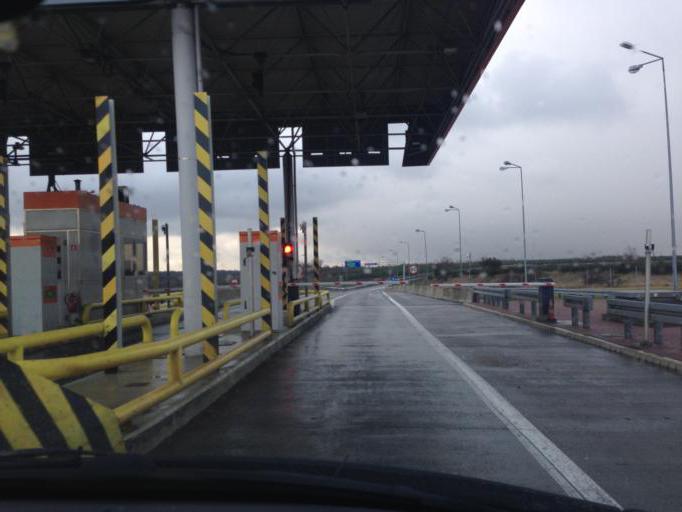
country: PL
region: Opole Voivodeship
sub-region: Powiat strzelecki
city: Ujazd
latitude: 50.4491
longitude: 18.3474
